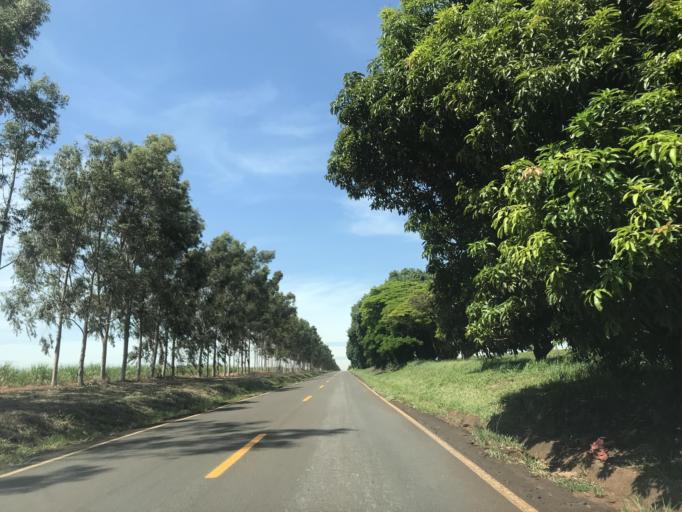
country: BR
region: Parana
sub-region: Paranavai
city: Nova Aurora
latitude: -22.8260
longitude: -52.6555
